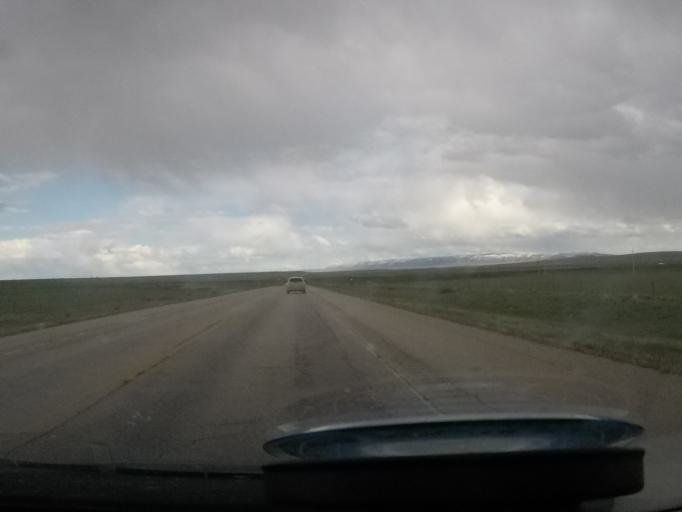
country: US
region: Wyoming
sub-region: Natrona County
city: Mills
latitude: 42.9544
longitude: -106.6440
